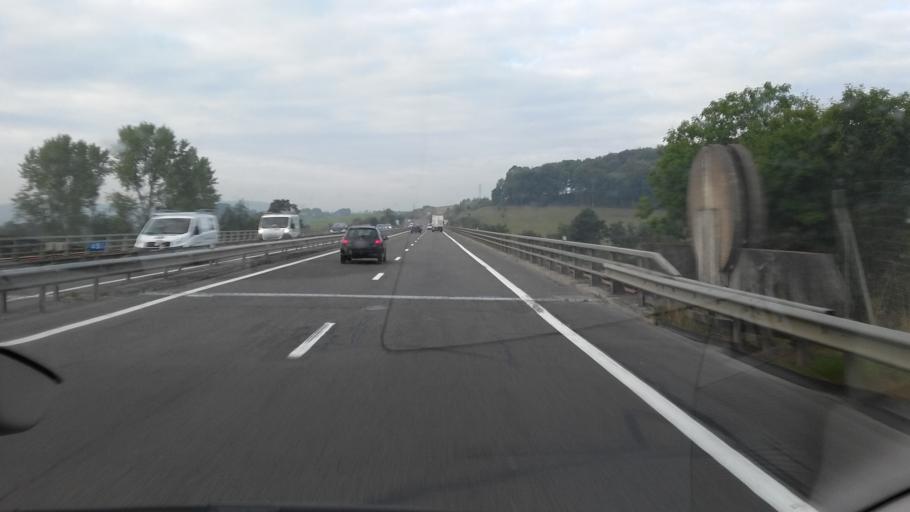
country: FR
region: Champagne-Ardenne
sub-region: Departement des Ardennes
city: La Francheville
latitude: 49.6671
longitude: 4.6426
